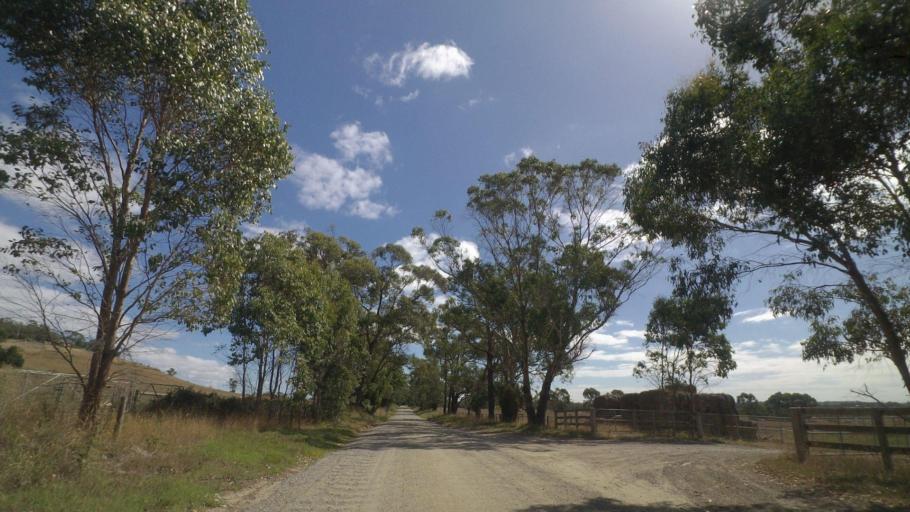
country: AU
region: Victoria
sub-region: Cardinia
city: Bunyip
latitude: -38.3265
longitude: 145.7145
